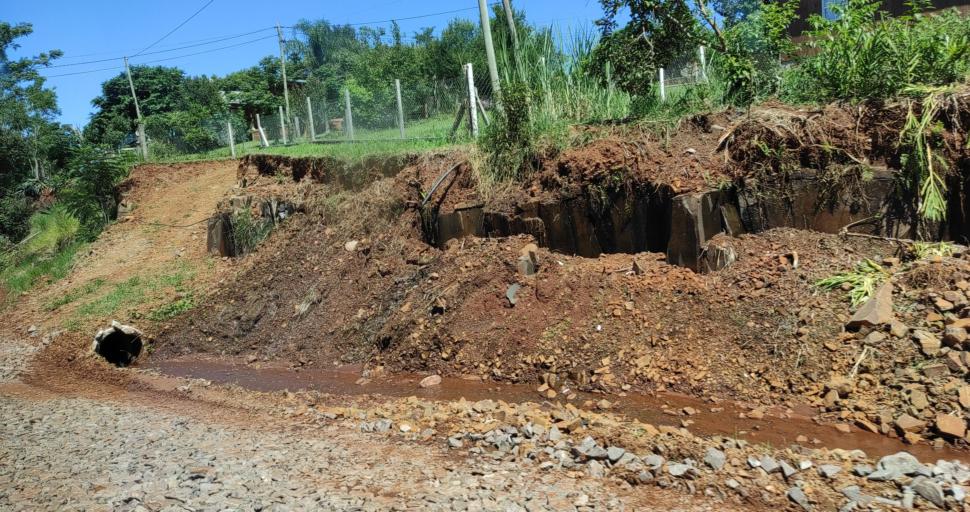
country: AR
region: Misiones
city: El Soberbio
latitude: -27.2880
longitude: -54.2163
